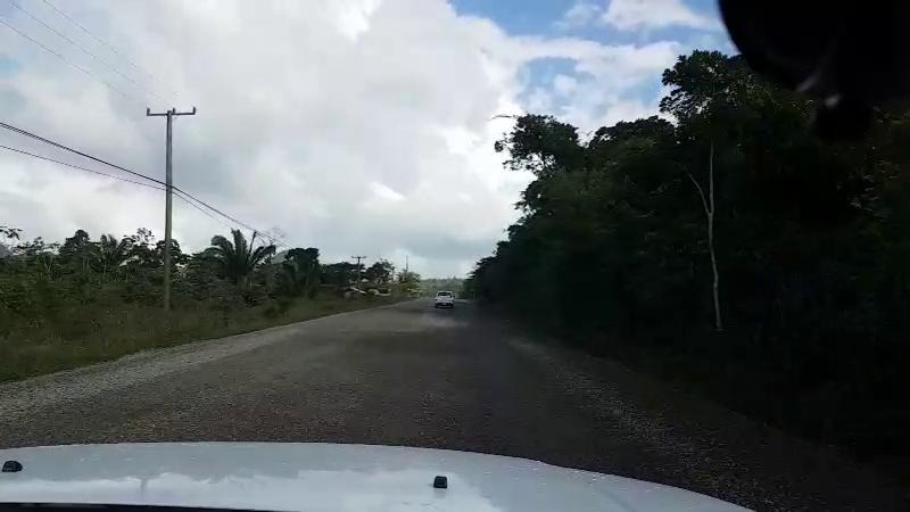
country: BZ
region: Cayo
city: Belmopan
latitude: 17.0882
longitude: -88.6161
